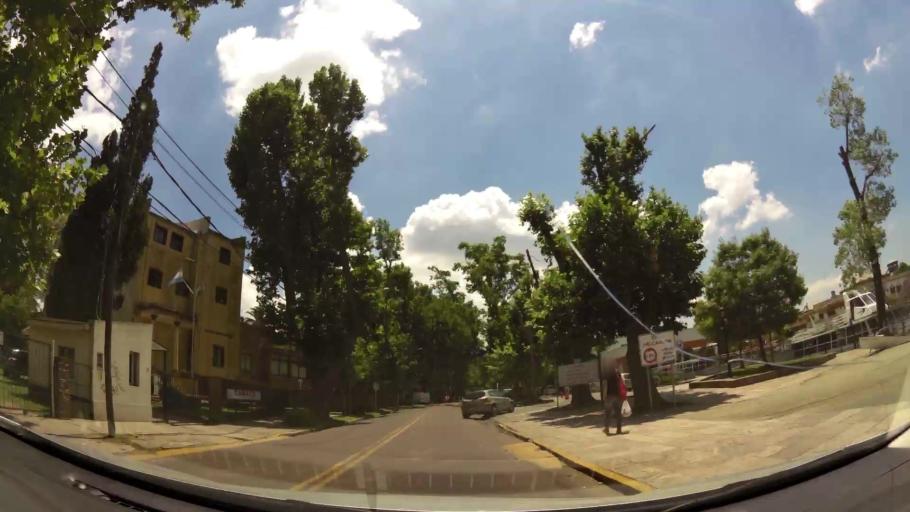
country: AR
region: Buenos Aires
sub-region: Partido de Tigre
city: Tigre
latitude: -34.4187
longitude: -58.5797
